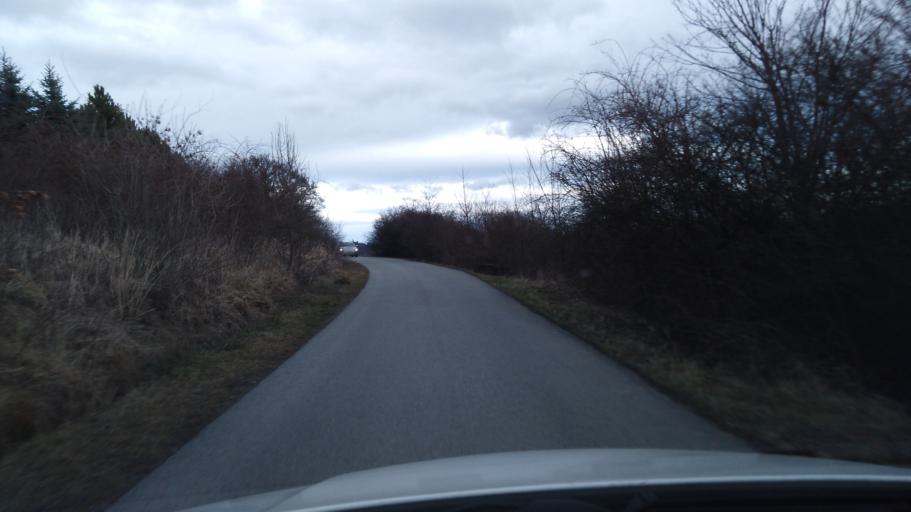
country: PL
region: Silesian Voivodeship
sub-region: Powiat zywiecki
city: Trzebinia
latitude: 49.6608
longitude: 19.2118
